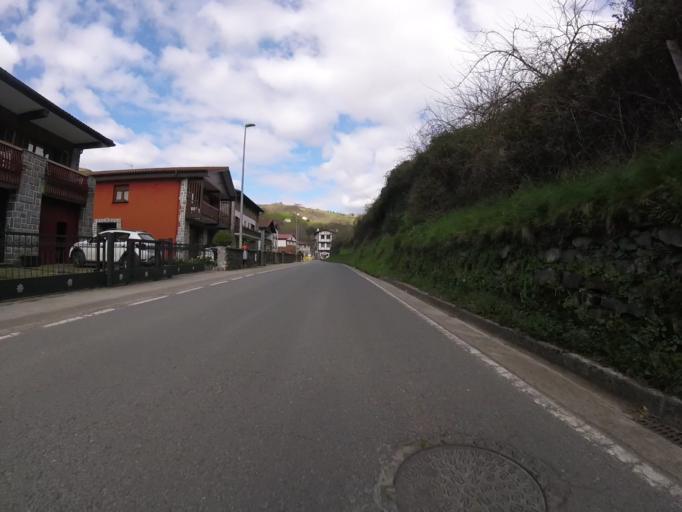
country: ES
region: Navarre
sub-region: Provincia de Navarra
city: Goizueta
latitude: 43.1696
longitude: -1.8624
